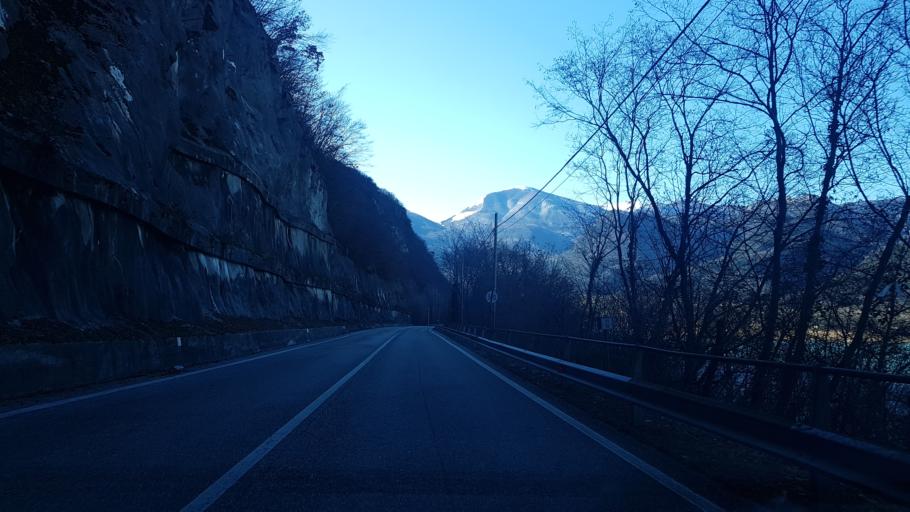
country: IT
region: Friuli Venezia Giulia
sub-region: Provincia di Udine
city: Bordano
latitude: 46.3259
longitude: 13.0784
